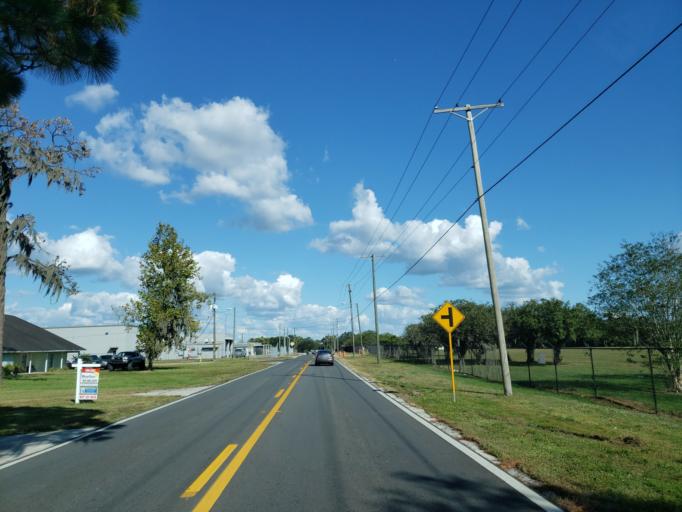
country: US
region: Florida
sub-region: Hillsborough County
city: Plant City
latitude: 28.0033
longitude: -82.1579
